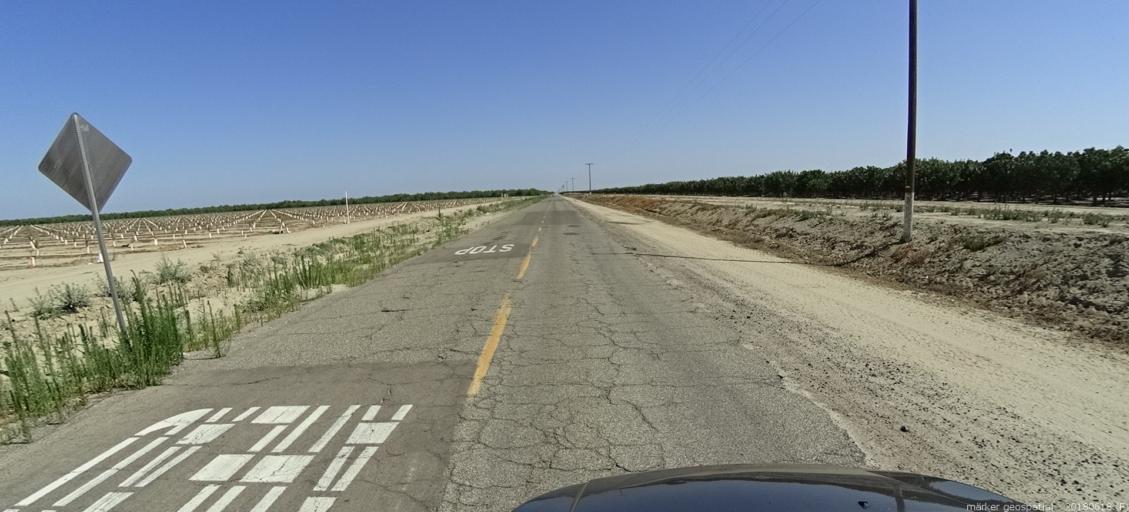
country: US
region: California
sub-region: Fresno County
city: Mendota
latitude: 36.8378
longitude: -120.2551
